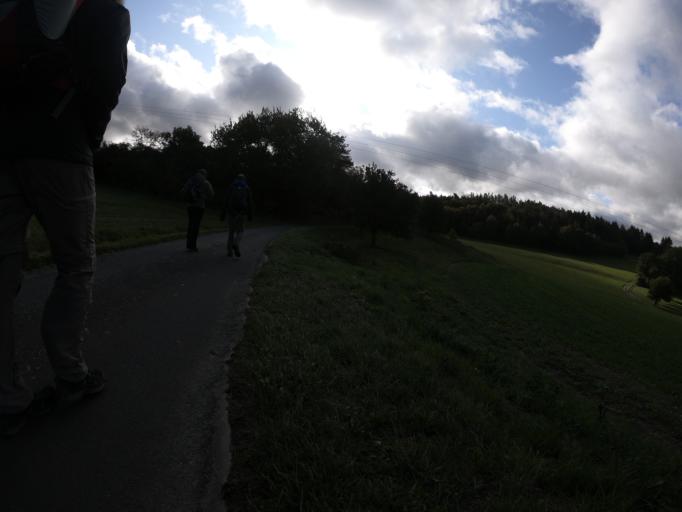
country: DE
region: Hesse
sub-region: Regierungsbezirk Darmstadt
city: Idstein
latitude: 50.2206
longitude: 8.2445
